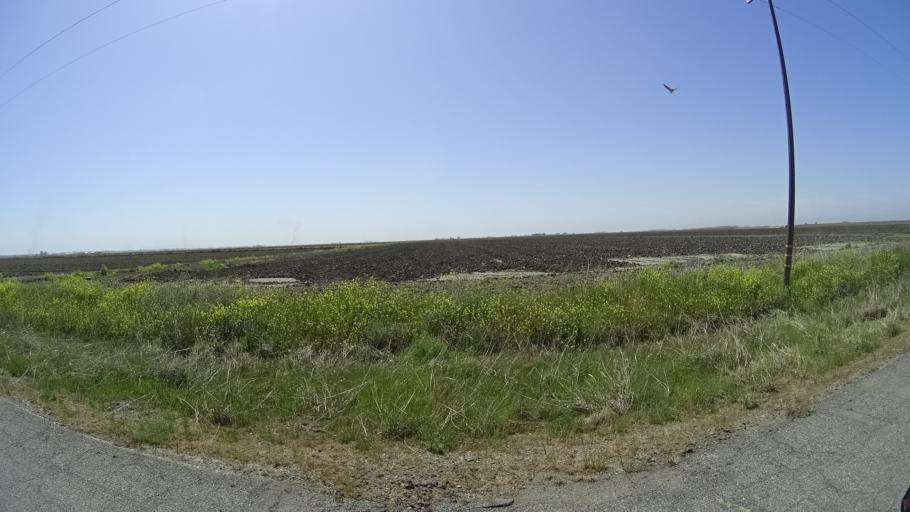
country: US
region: California
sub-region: Glenn County
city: Willows
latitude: 39.4929
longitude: -122.0726
